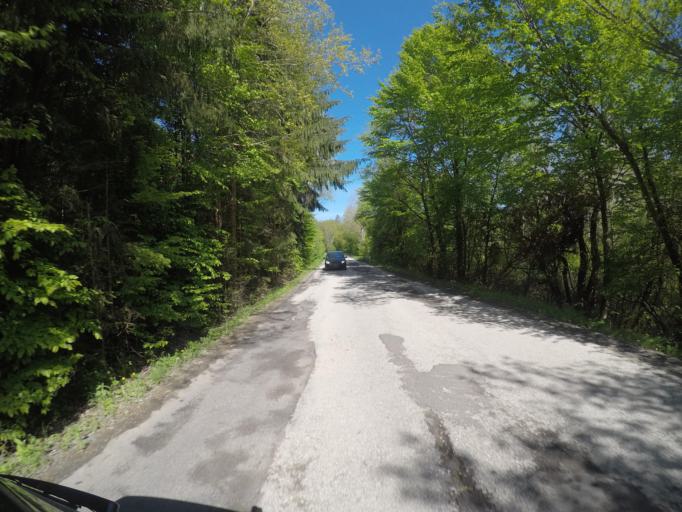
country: SK
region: Banskobystricky
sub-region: Okres Banska Bystrica
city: Zvolen
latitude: 48.5857
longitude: 19.0661
